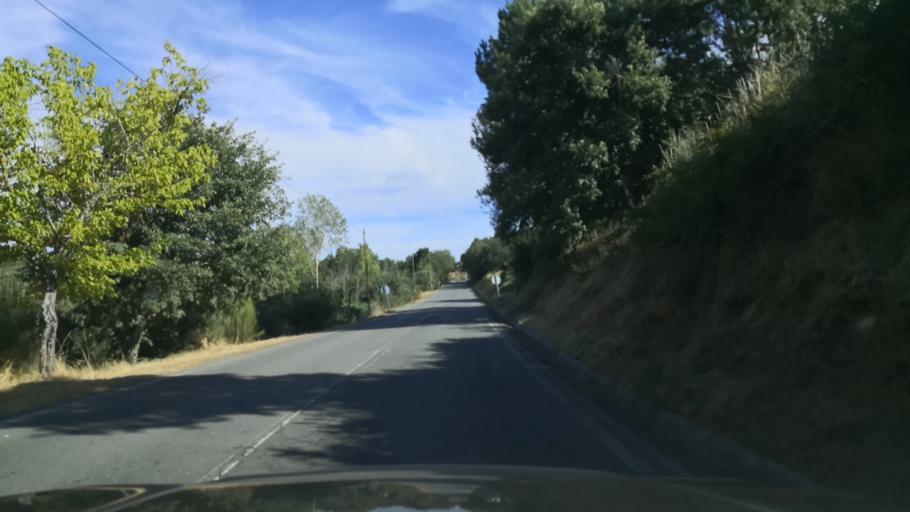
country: PT
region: Vila Real
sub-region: Murca
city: Murca
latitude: 41.3776
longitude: -7.5465
